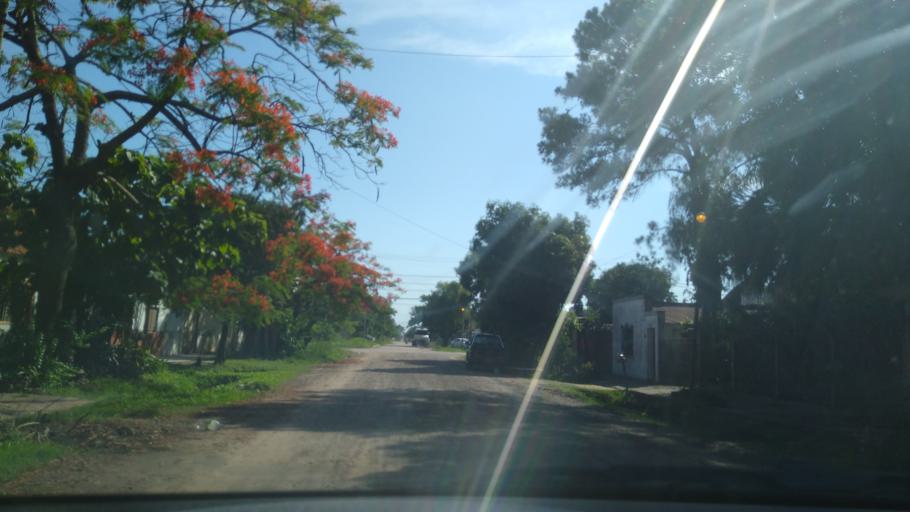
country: AR
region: Chaco
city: Barranqueras
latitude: -27.4851
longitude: -58.9473
